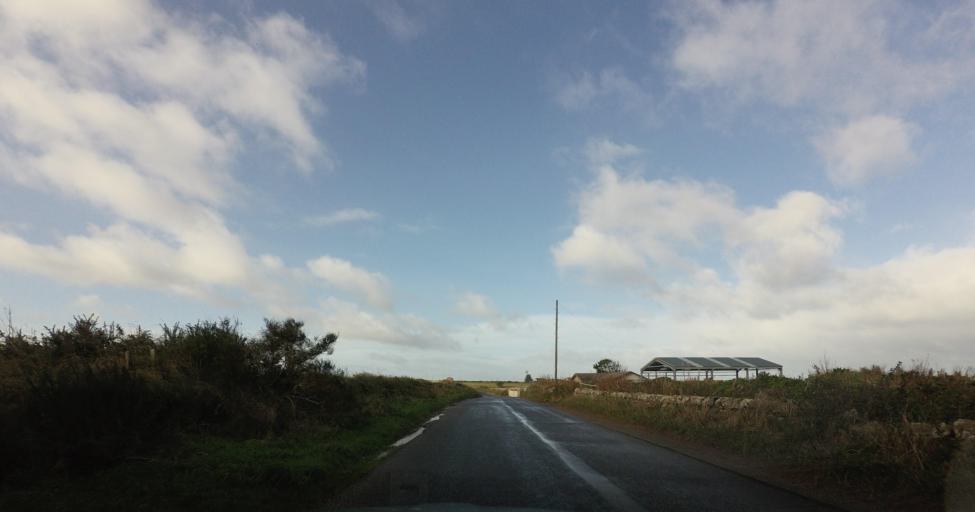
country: GB
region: Scotland
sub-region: Aberdeenshire
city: Whitehills
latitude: 57.6706
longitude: -2.5857
